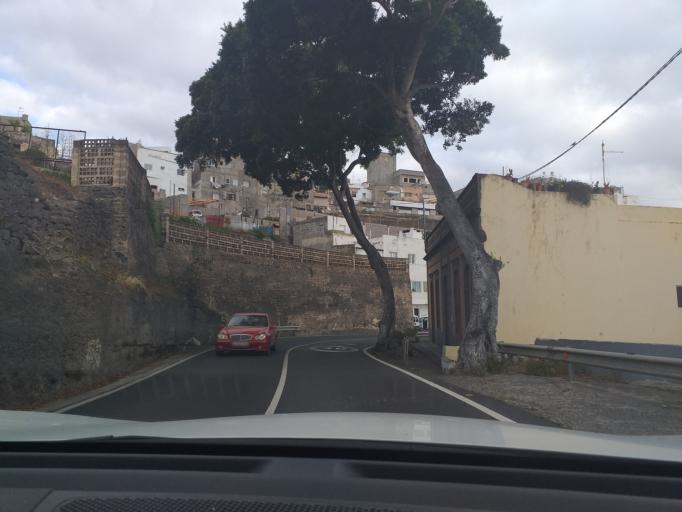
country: ES
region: Canary Islands
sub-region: Provincia de Las Palmas
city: Arucas
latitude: 28.1137
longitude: -15.4924
